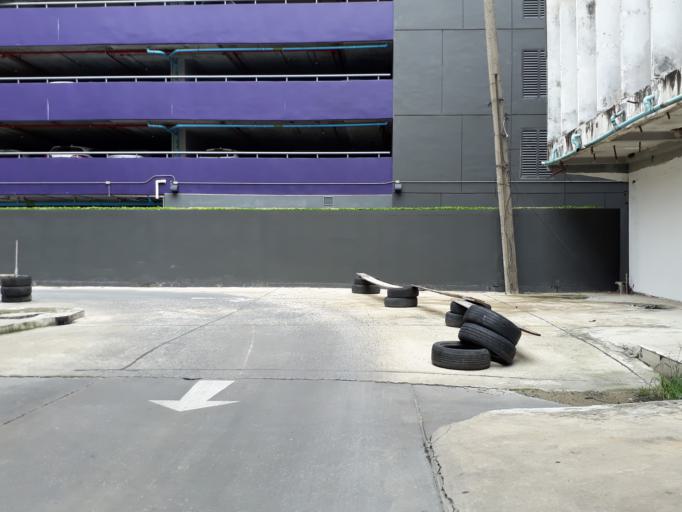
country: TH
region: Bangkok
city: Din Daeng
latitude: 13.7507
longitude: 100.5573
